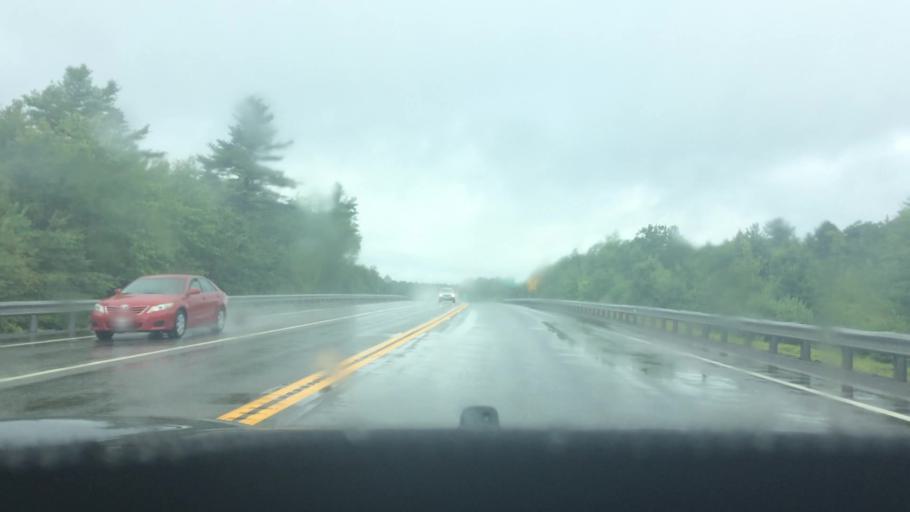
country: US
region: Massachusetts
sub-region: Worcester County
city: South Ashburnham
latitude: 42.5961
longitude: -71.9656
